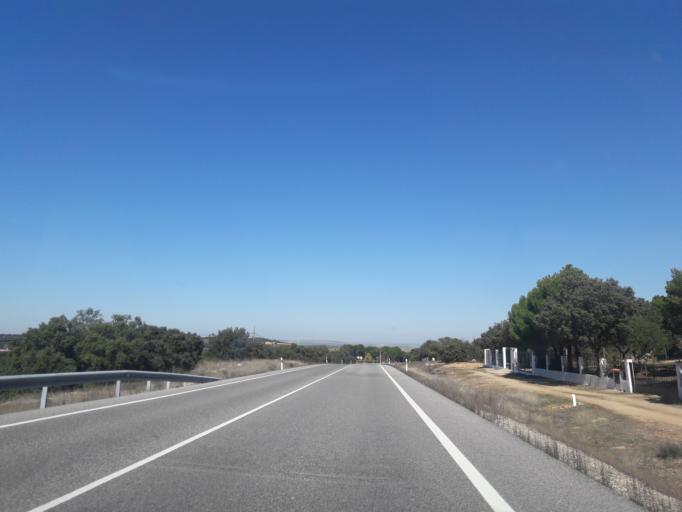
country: ES
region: Castille and Leon
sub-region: Provincia de Salamanca
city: Mozarbez
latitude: 40.8240
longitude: -5.6371
